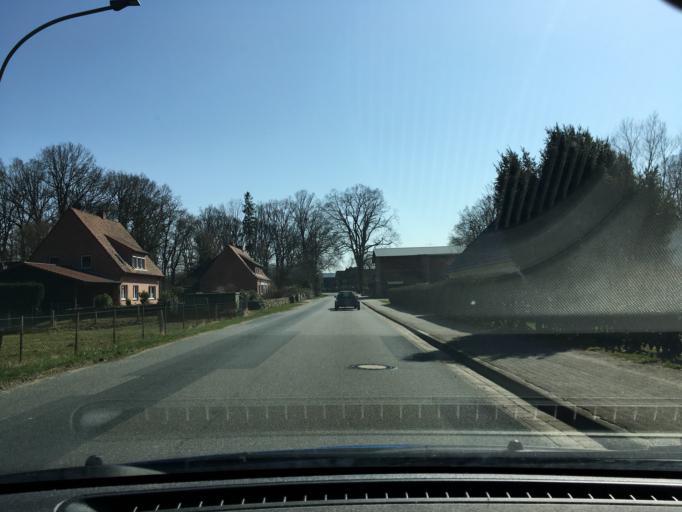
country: DE
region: Lower Saxony
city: Wriedel
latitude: 53.0533
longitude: 10.2912
